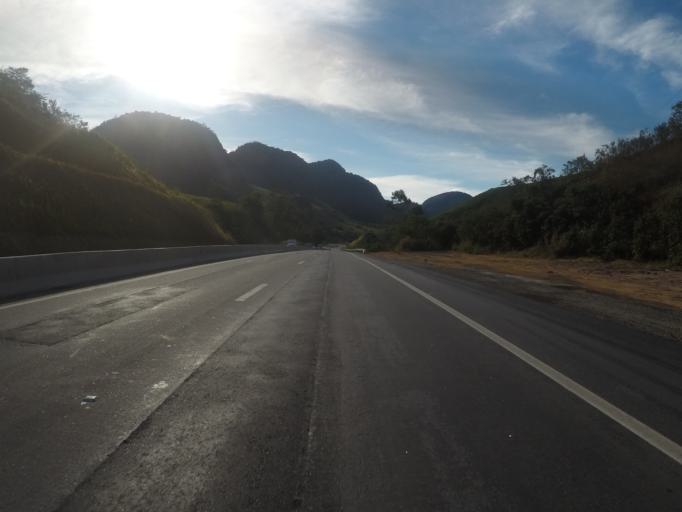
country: BR
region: Espirito Santo
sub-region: Ibiracu
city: Ibiracu
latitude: -19.8482
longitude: -40.3838
